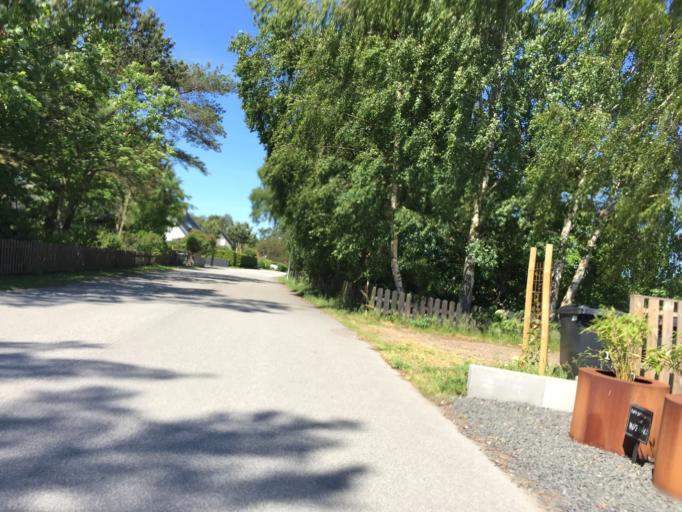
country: SE
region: Skane
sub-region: Trelleborgs Kommun
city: Anderslov
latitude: 55.3499
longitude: 13.2632
